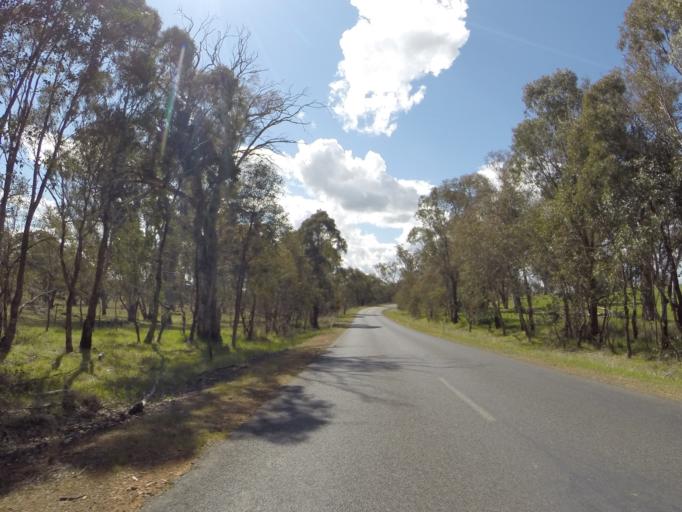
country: AU
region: New South Wales
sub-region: Yass Valley
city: Yass
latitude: -34.9755
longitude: 148.8560
